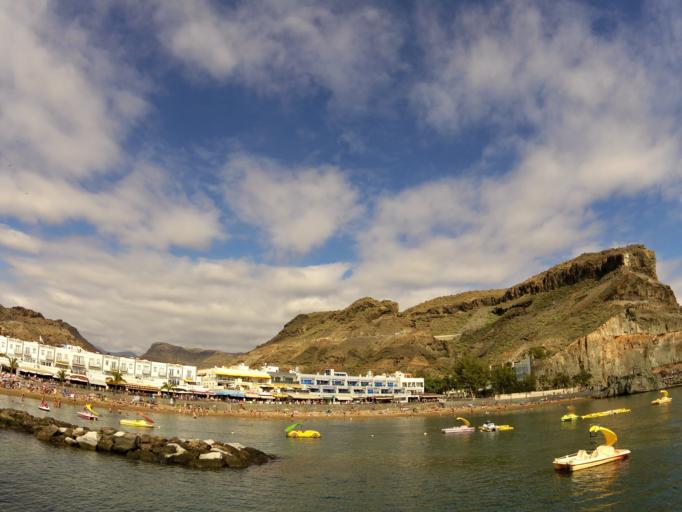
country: ES
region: Canary Islands
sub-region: Provincia de Las Palmas
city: Puerto Rico
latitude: 27.8173
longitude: -15.7639
